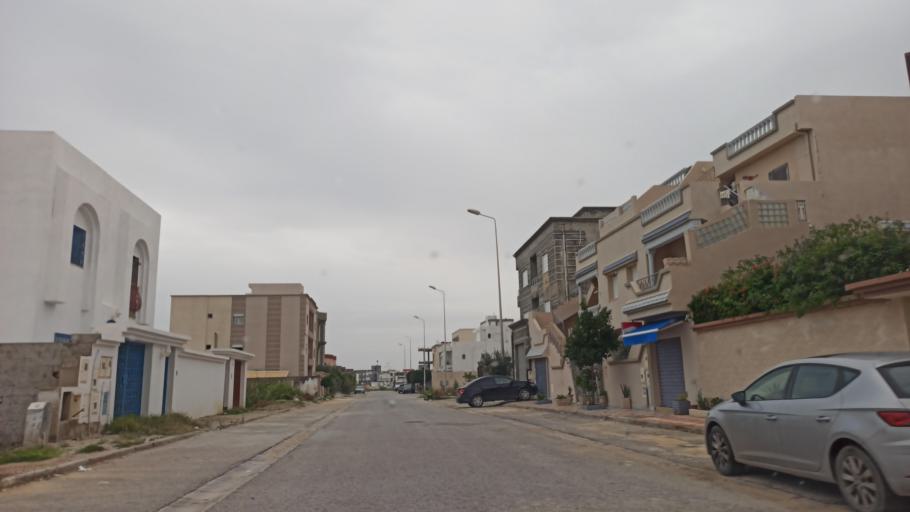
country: TN
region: Tunis
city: Hammam-Lif
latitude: 36.7107
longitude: 10.4136
